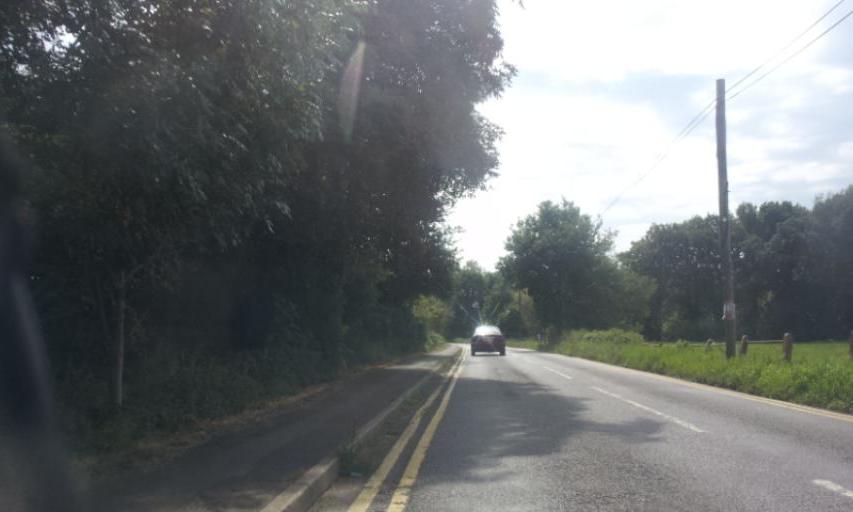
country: GB
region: England
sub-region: Kent
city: Yalding
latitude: 51.2204
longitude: 0.4217
